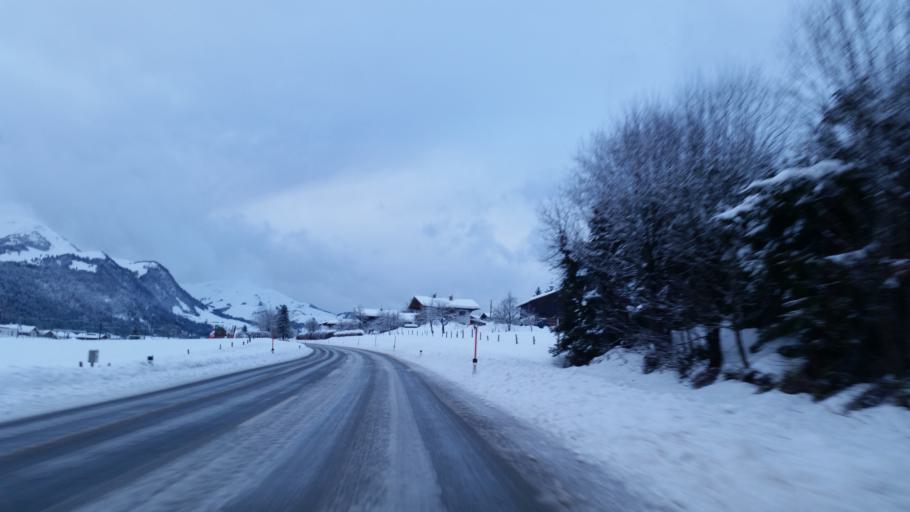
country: AT
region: Tyrol
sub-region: Politischer Bezirk Kitzbuhel
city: Hochfilzen
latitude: 47.4678
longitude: 12.5859
